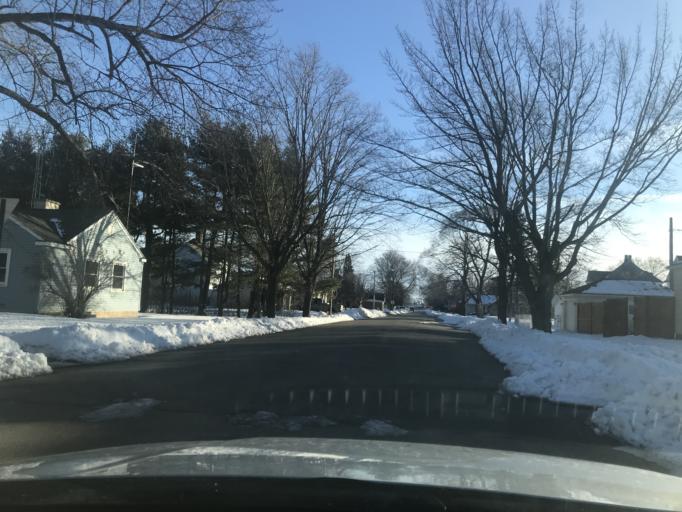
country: US
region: Michigan
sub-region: Menominee County
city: Menominee
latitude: 45.1125
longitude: -87.6265
